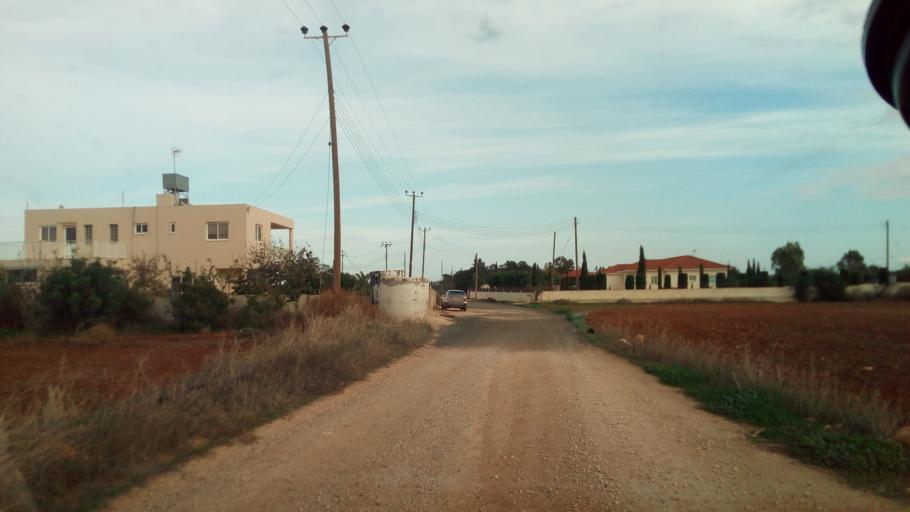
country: CY
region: Ammochostos
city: Avgorou
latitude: 35.0573
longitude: 33.8760
